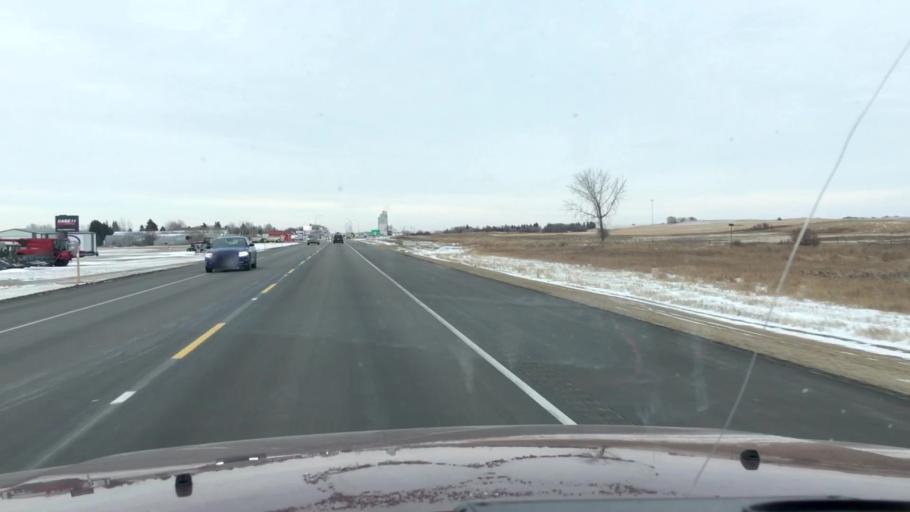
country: CA
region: Saskatchewan
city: Moose Jaw
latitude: 50.8558
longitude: -105.5776
